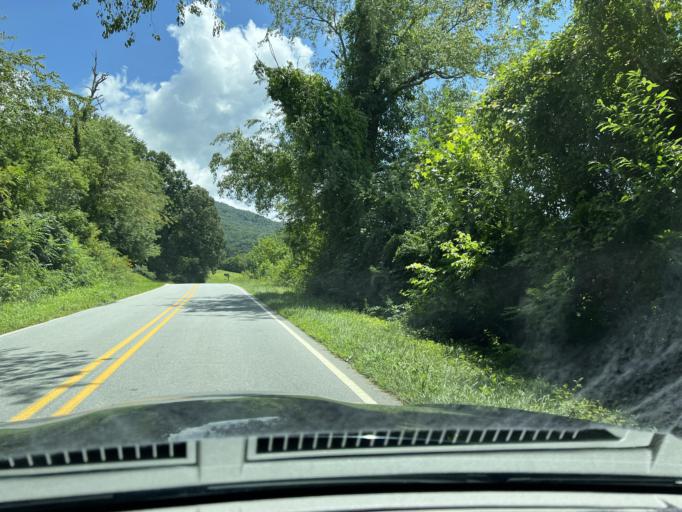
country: US
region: North Carolina
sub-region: Henderson County
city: Hoopers Creek
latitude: 35.4374
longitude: -82.4356
